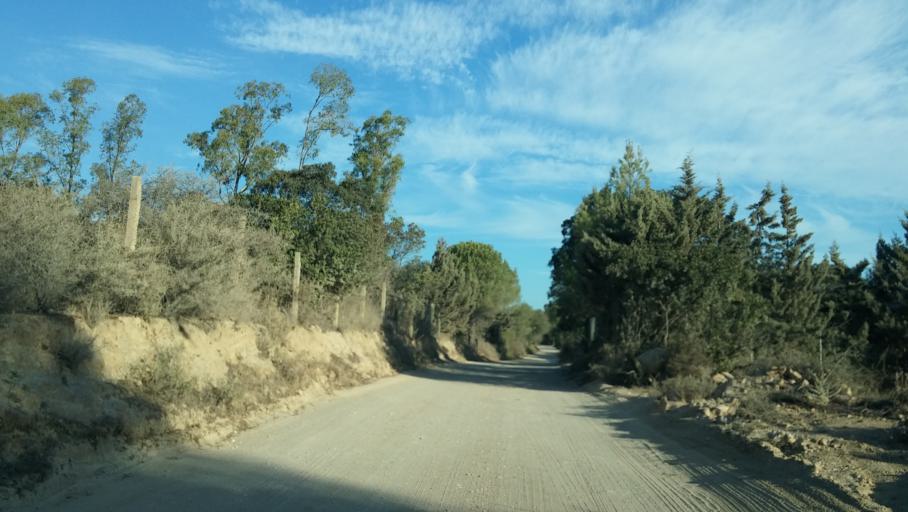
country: IT
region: Sardinia
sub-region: Provincia di Nuoro
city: La Caletta
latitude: 40.4844
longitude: 9.8018
